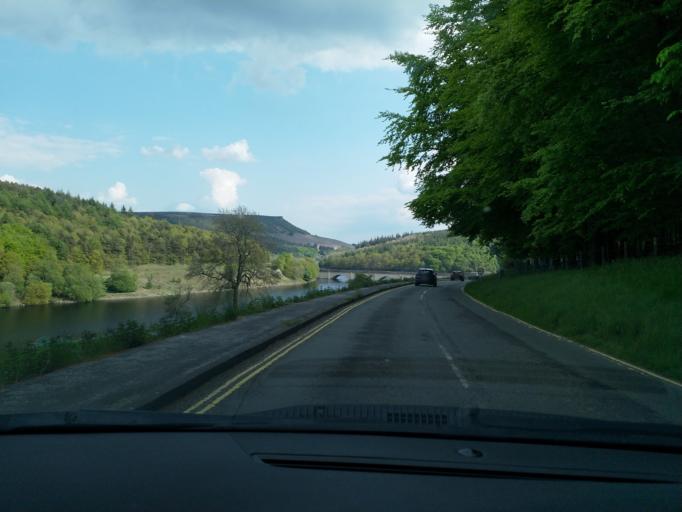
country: GB
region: England
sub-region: Derbyshire
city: Hope Valley
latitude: 53.3793
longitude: -1.7150
